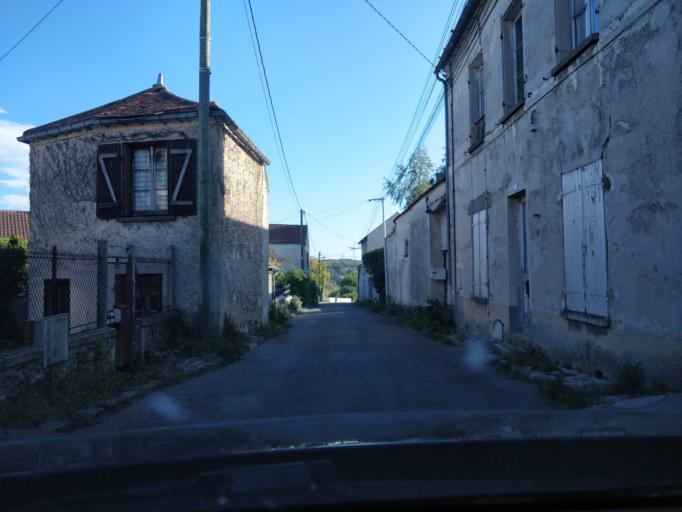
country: FR
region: Ile-de-France
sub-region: Departement de l'Essonne
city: Limours
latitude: 48.6260
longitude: 2.0735
